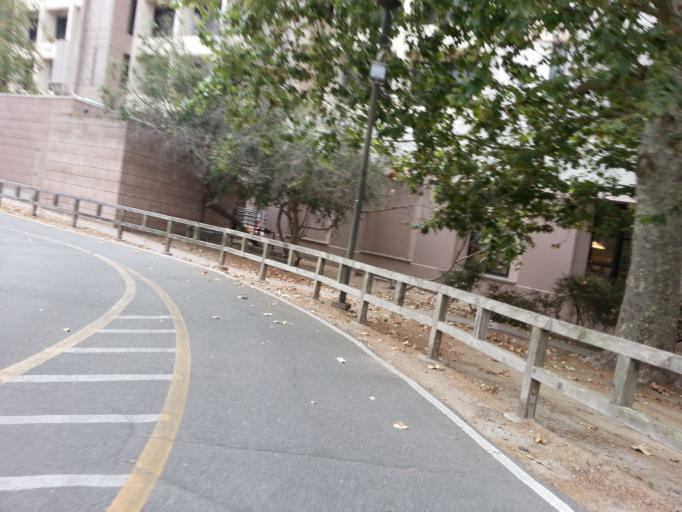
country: US
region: California
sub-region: Santa Barbara County
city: Isla Vista
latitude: 34.4158
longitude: -119.8433
